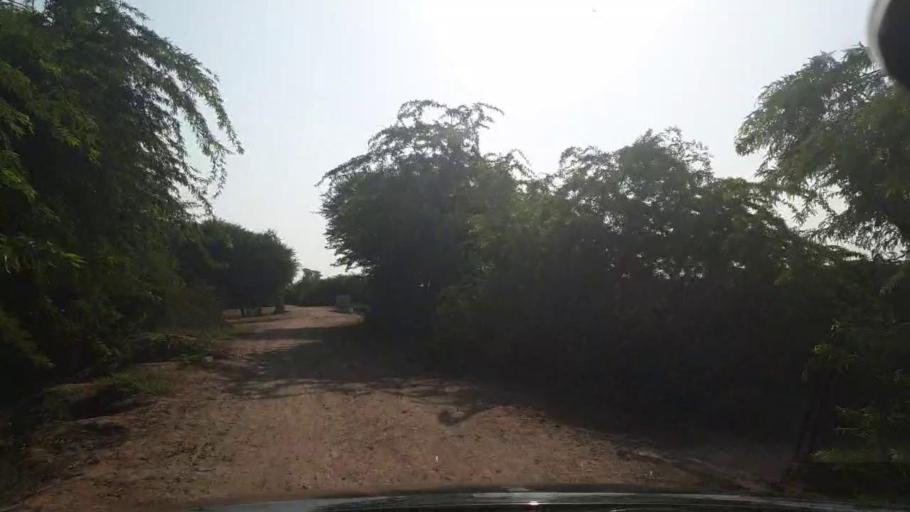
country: PK
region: Sindh
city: Tando Bago
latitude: 24.6508
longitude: 69.1741
